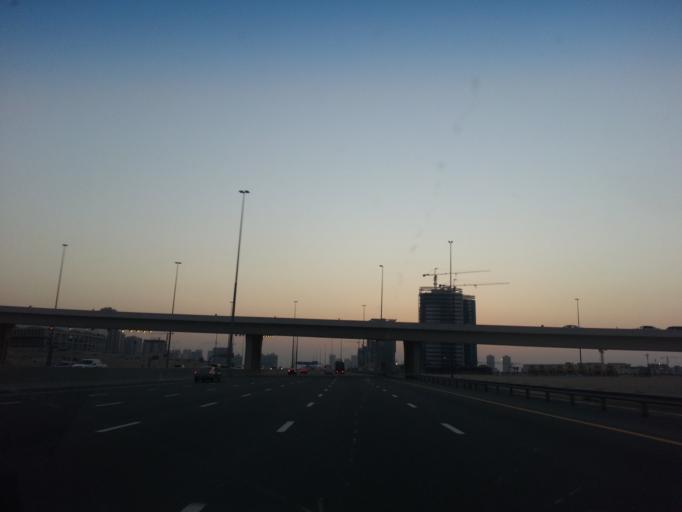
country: AE
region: Dubai
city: Dubai
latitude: 25.0518
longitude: 55.2229
